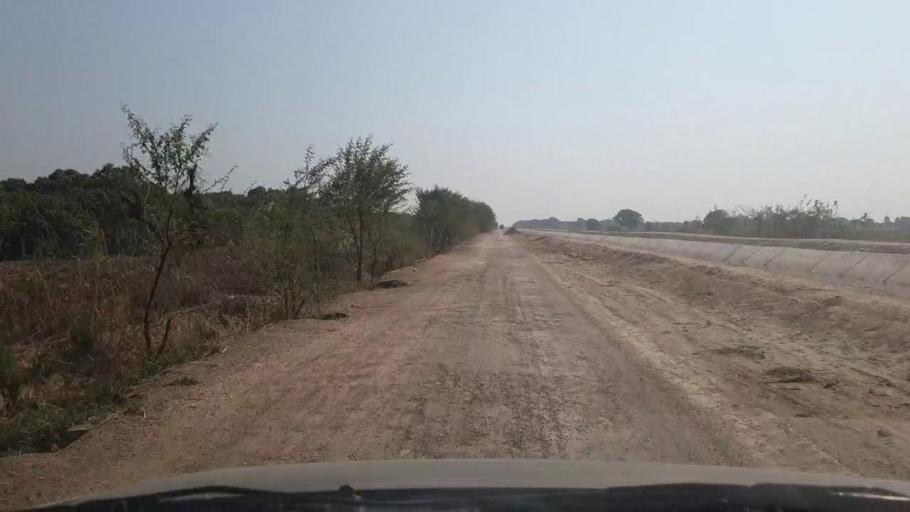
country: PK
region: Sindh
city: Mirwah Gorchani
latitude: 25.2564
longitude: 69.1214
